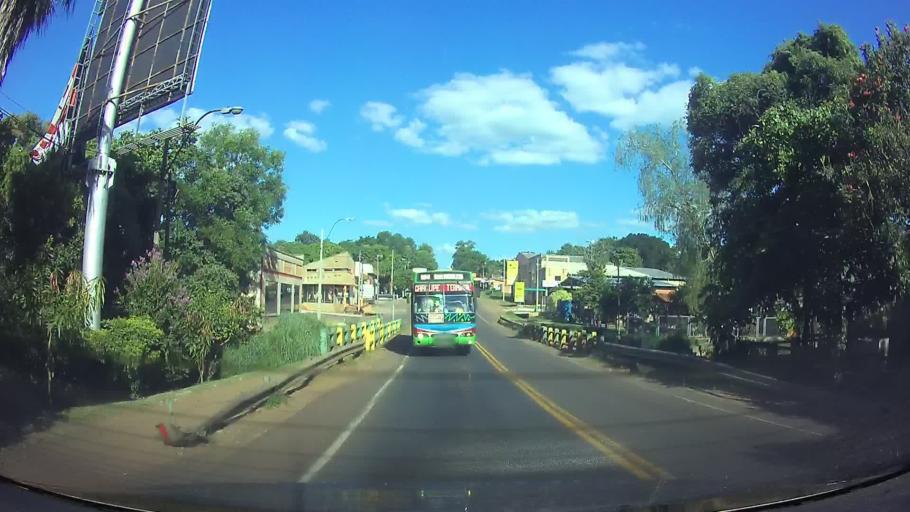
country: PY
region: Cordillera
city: Caacupe
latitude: -25.3829
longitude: -57.1340
